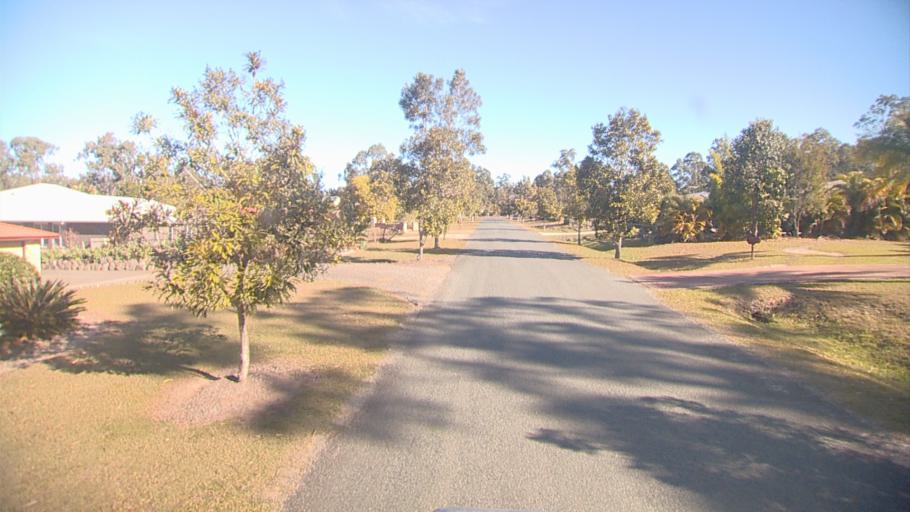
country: AU
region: Queensland
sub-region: Ipswich
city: Springfield Lakes
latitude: -27.7310
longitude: 152.9235
